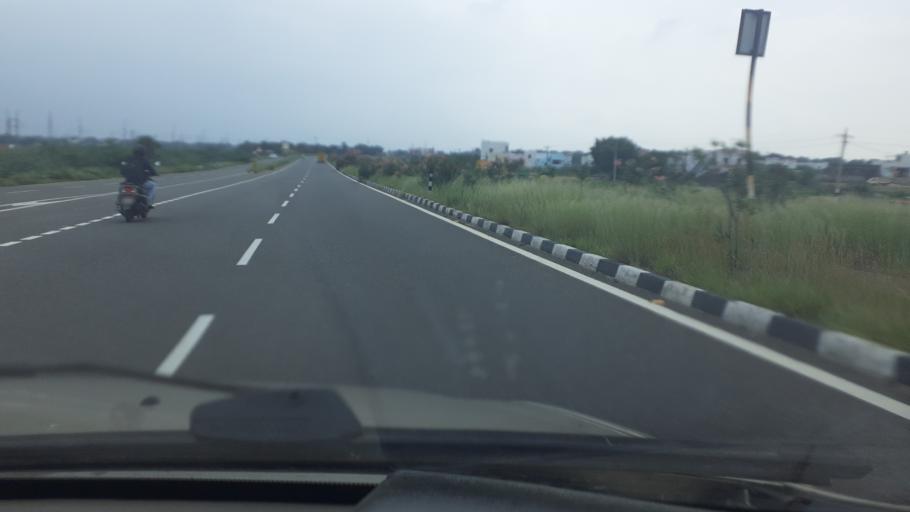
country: IN
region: Tamil Nadu
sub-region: Madurai
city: Tirupparangunram
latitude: 9.8004
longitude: 77.9841
